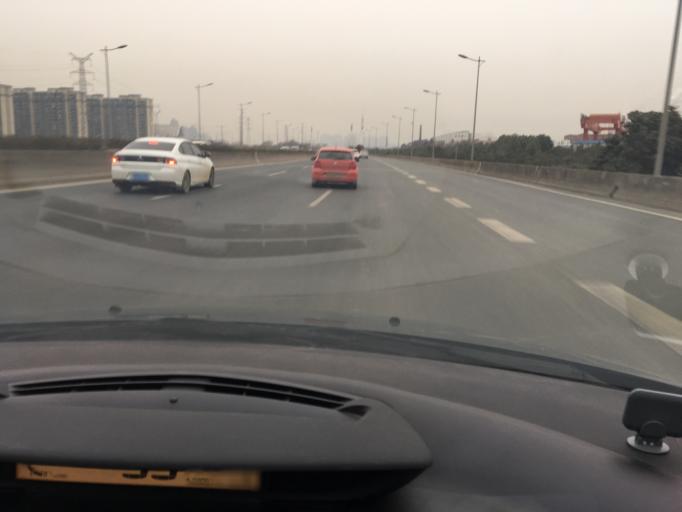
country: CN
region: Hubei
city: Hongqi
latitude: 30.6000
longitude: 114.4270
